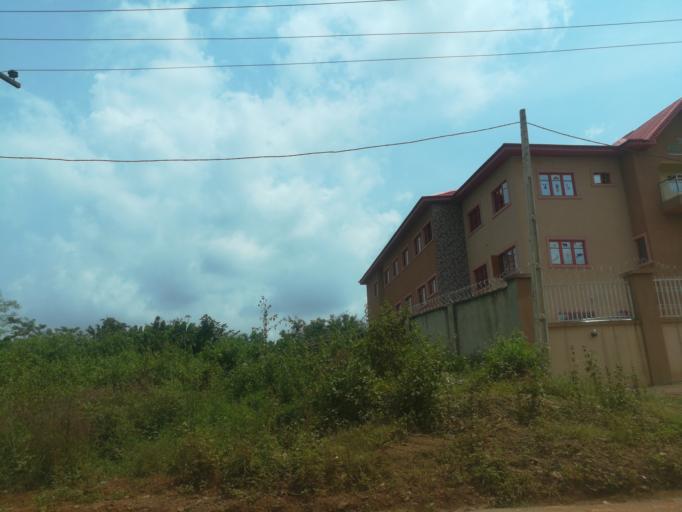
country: NG
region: Oyo
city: Moniya
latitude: 7.4670
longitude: 3.9546
